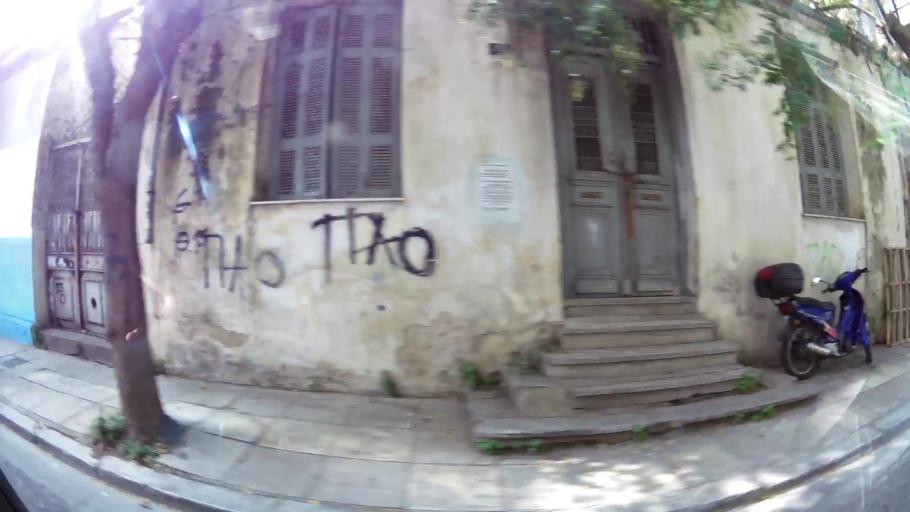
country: GR
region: Attica
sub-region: Nomarchia Athinas
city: Athens
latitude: 37.9924
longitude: 23.7098
